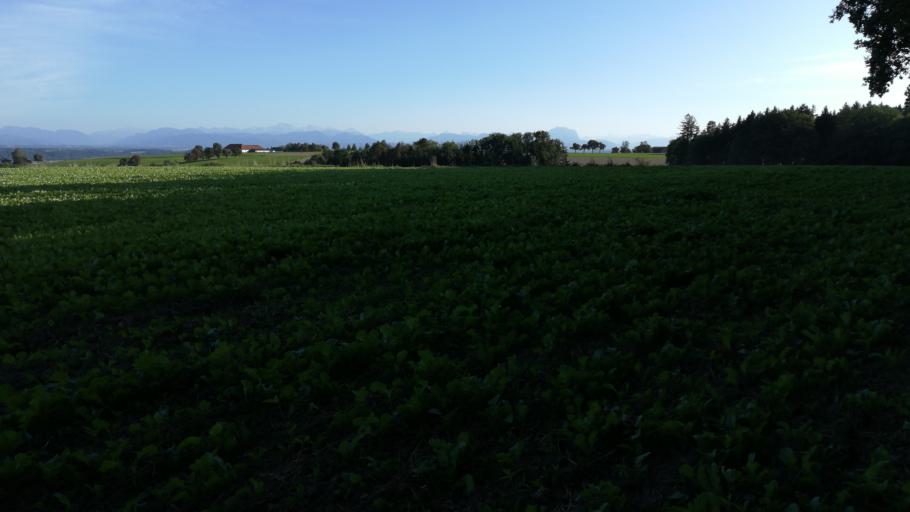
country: AT
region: Upper Austria
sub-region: Wels-Land
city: Gunskirchen
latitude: 48.1696
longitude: 13.9267
